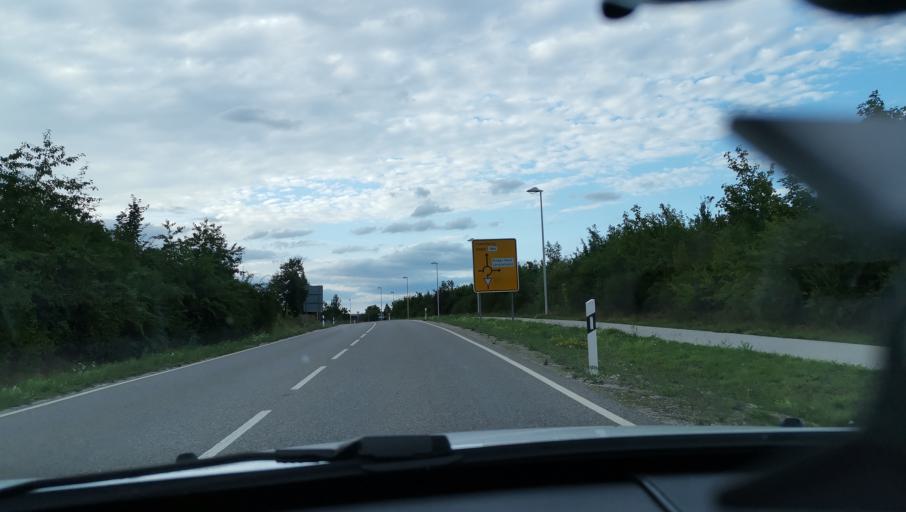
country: DE
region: Bavaria
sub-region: Regierungsbezirk Mittelfranken
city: Zirndorf
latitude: 49.4380
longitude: 10.9382
